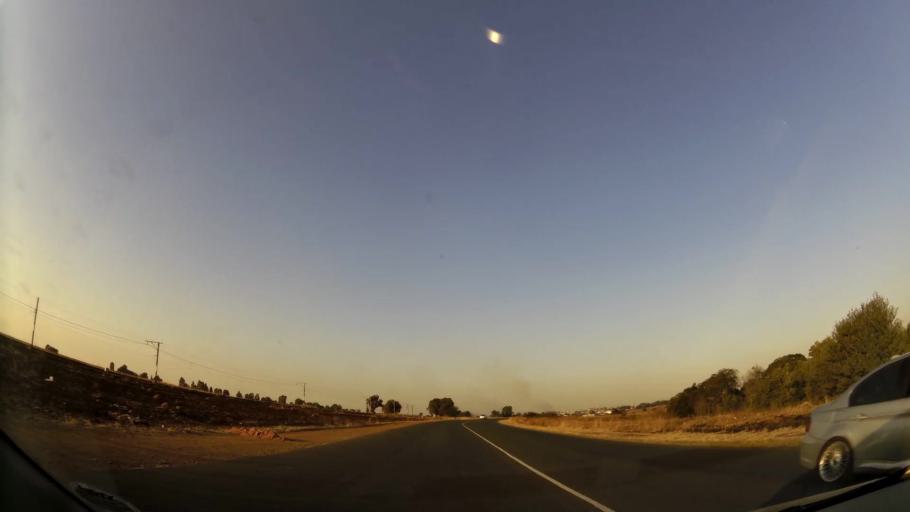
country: ZA
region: Gauteng
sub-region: West Rand District Municipality
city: Randfontein
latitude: -26.2027
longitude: 27.6697
